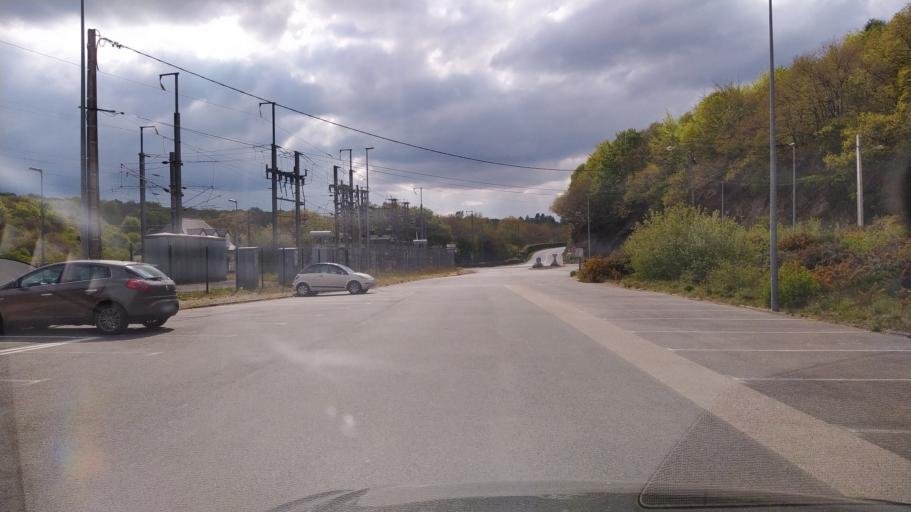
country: FR
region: Brittany
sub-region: Departement du Finistere
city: Landivisiau
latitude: 48.4961
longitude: -4.0822
